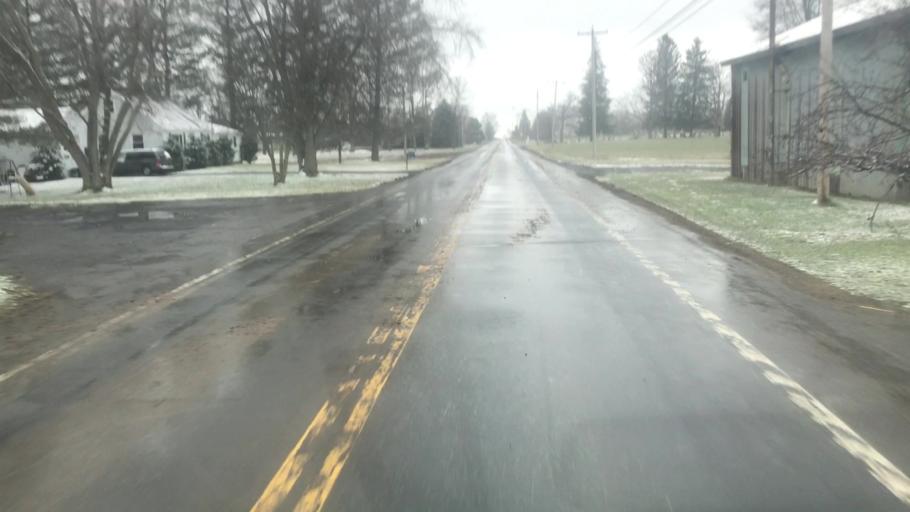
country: US
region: New York
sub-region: Onondaga County
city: Marcellus
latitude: 42.9948
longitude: -76.3915
